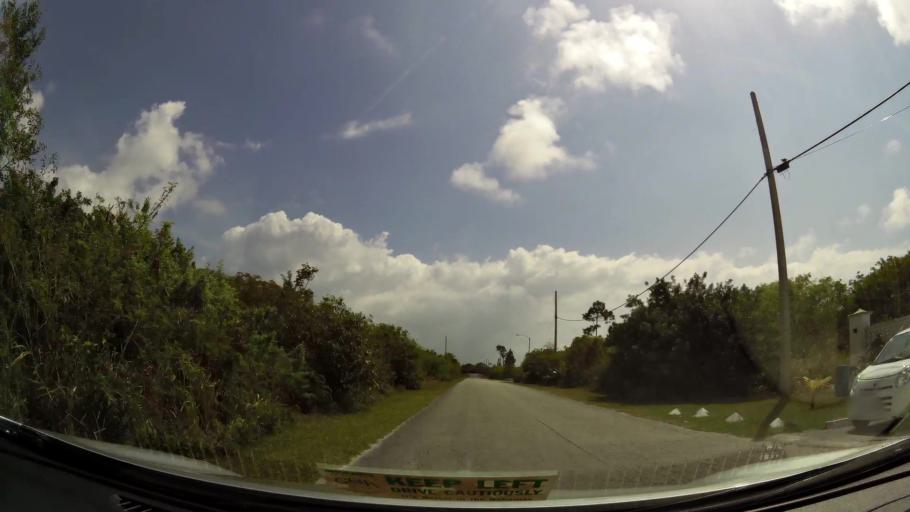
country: BS
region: Freeport
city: Freeport
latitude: 26.5120
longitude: -78.7145
